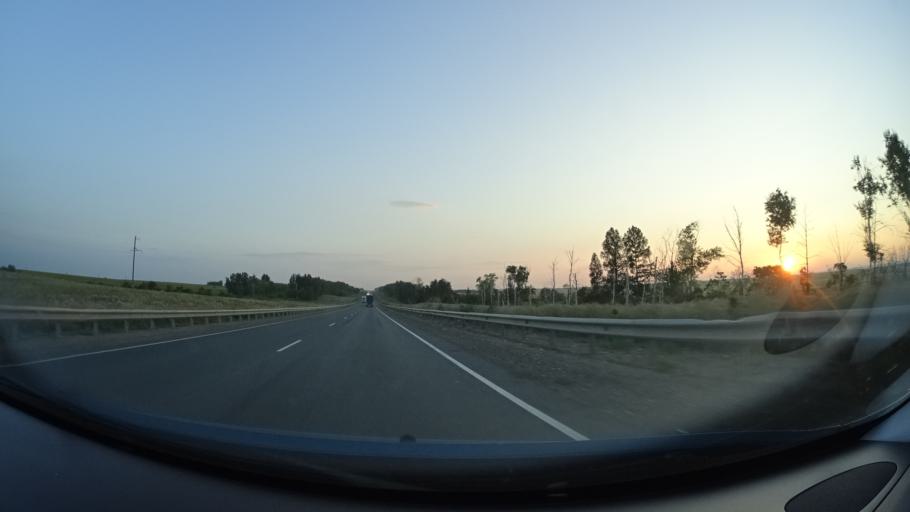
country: RU
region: Samara
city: Sukhodol
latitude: 53.8450
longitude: 51.1253
